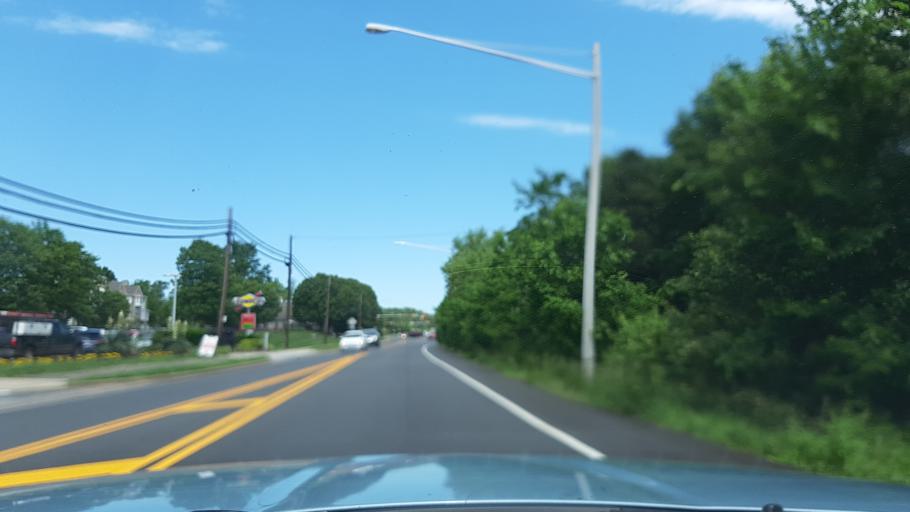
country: US
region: Virginia
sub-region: Fairfax County
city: Newington
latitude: 38.7402
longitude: -77.2114
